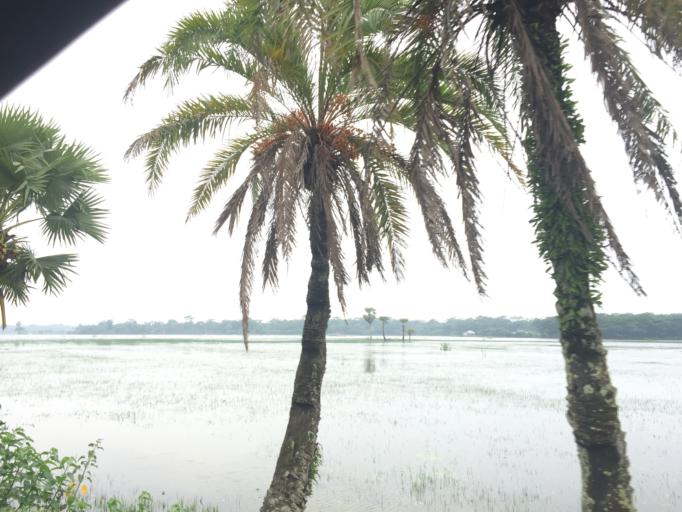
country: BD
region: Barisal
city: Mathba
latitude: 22.2129
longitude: 89.9219
